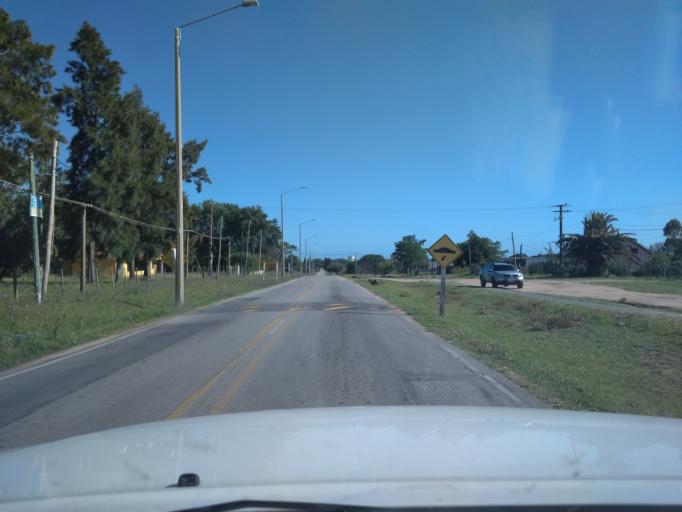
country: UY
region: Canelones
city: San Ramon
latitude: -34.3044
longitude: -55.9582
